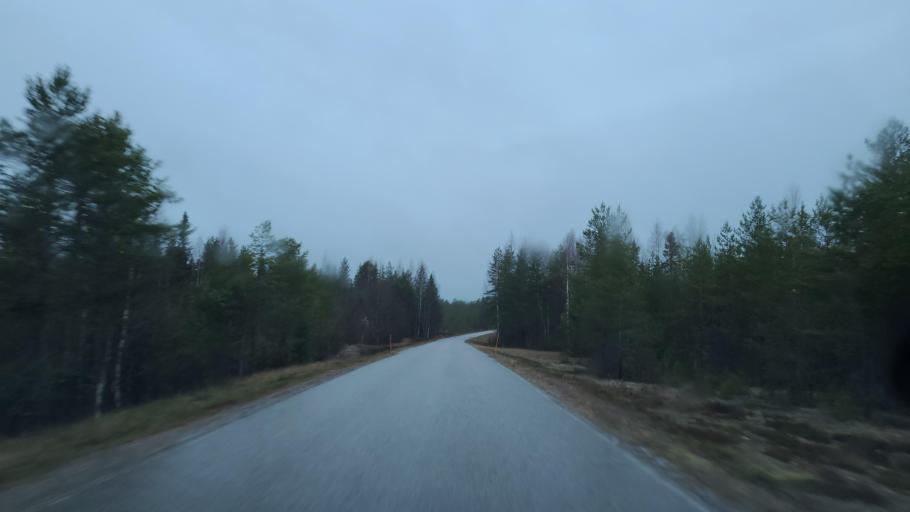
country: FI
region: Lapland
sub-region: Kemi-Tornio
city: Simo
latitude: 65.8663
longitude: 25.2241
